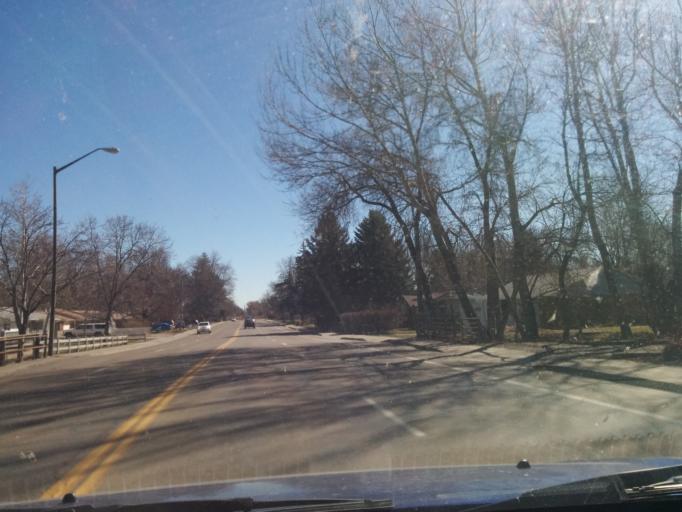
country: US
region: Colorado
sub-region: Larimer County
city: Fort Collins
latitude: 40.5820
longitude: -105.1105
